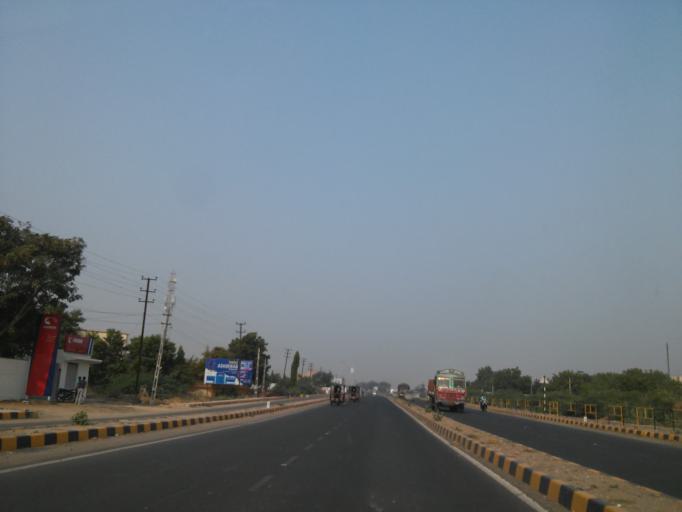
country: IN
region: Gujarat
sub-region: Kachchh
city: Bhuj
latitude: 23.2373
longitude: 69.7238
